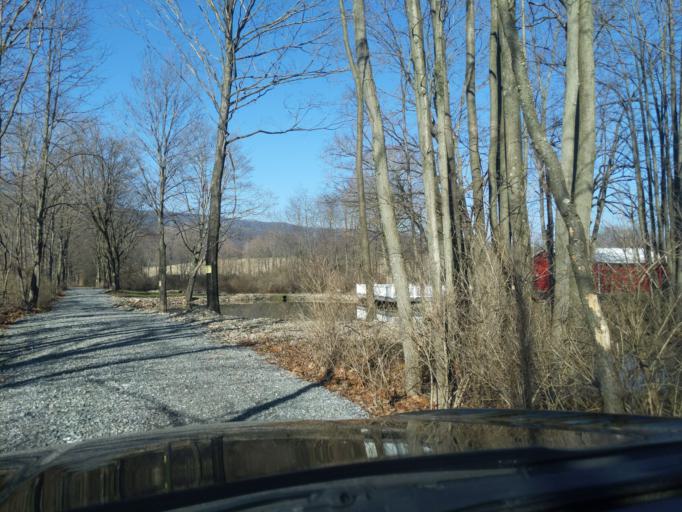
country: US
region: Pennsylvania
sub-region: Blair County
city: Bellwood
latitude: 40.5575
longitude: -78.2701
